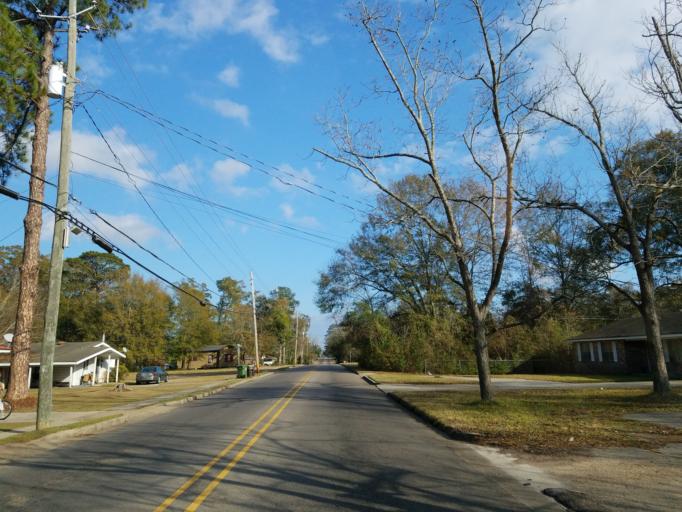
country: US
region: Mississippi
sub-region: Forrest County
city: Hattiesburg
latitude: 31.3357
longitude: -89.3218
